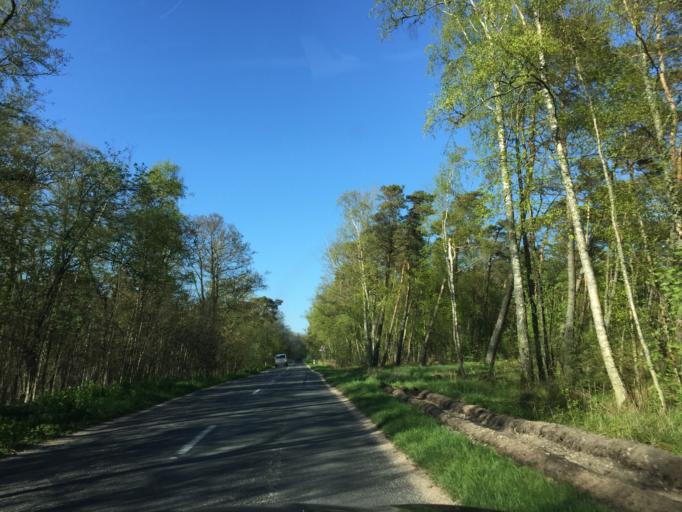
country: LT
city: Nida
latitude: 55.2114
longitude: 20.8795
